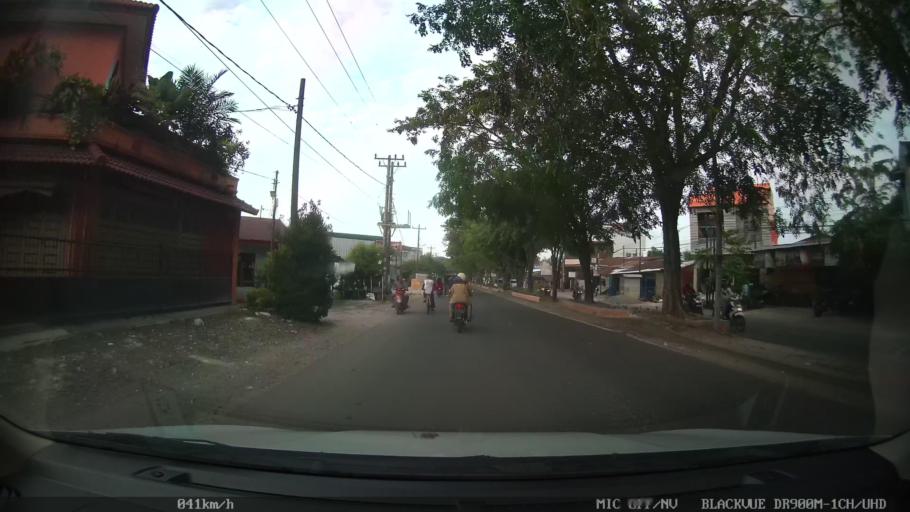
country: ID
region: North Sumatra
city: Sunggal
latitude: 3.5505
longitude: 98.6093
